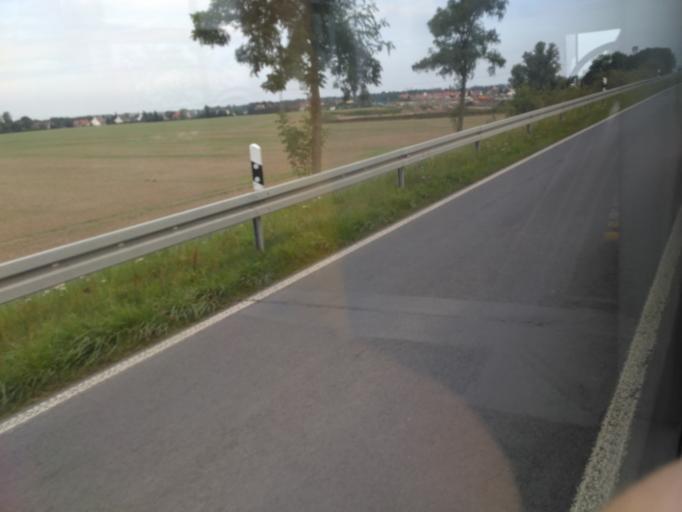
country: DE
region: Saxony
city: Grossenhain
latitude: 51.2736
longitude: 13.5198
